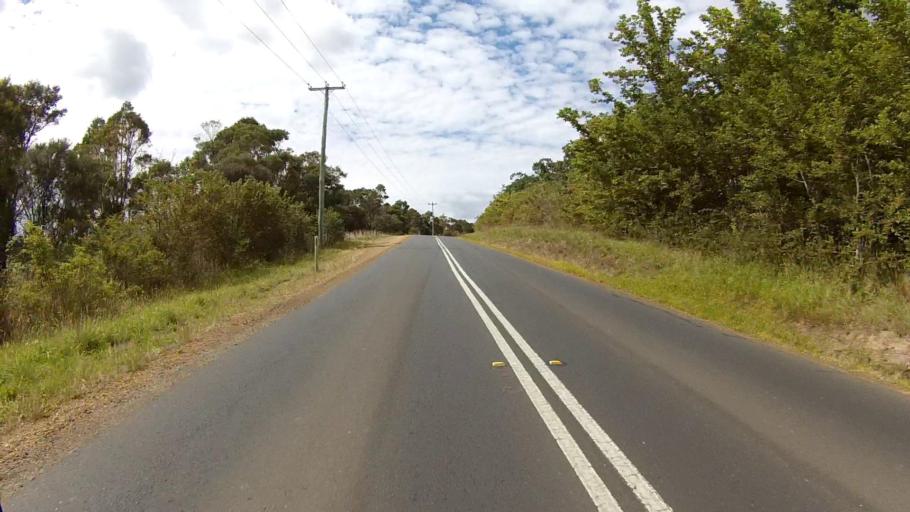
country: AU
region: Tasmania
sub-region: Clarence
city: Cambridge
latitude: -42.7986
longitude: 147.4215
